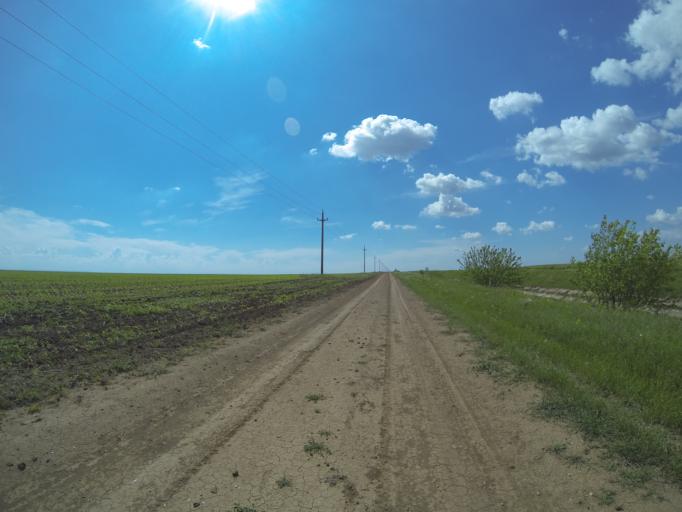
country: RO
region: Dolj
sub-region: Comuna Dranicu
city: Dranic
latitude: 44.0166
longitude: 23.7867
